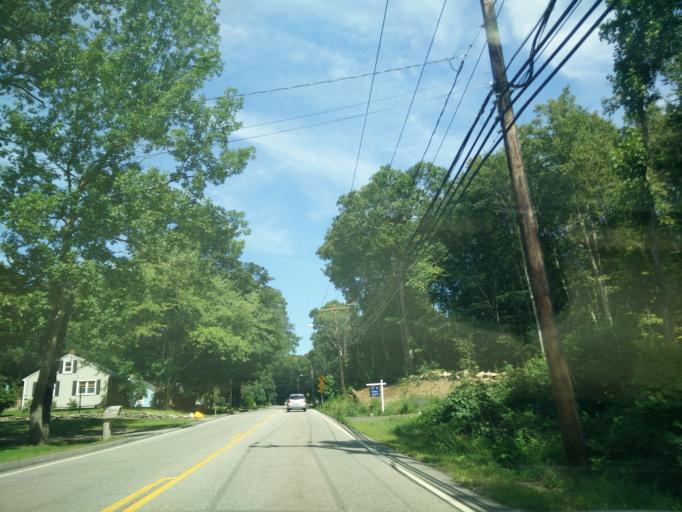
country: US
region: Connecticut
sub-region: Middlesex County
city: Clinton
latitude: 41.3025
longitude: -72.5336
